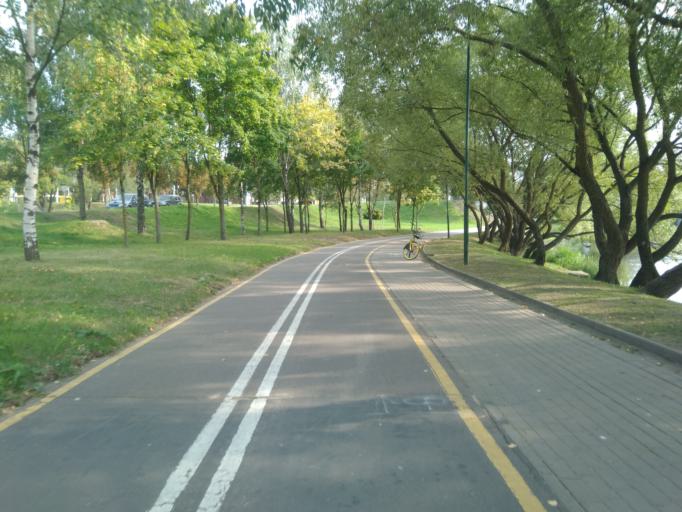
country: BY
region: Minsk
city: Minsk
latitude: 53.8753
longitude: 27.5841
